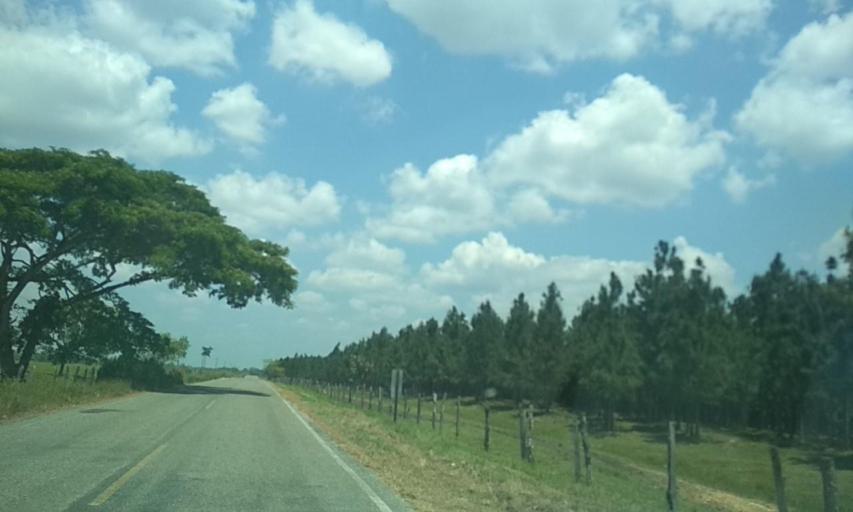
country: MX
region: Tabasco
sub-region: Huimanguillo
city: Huapacal 1ra. Seccion
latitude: 17.7562
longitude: -93.7678
